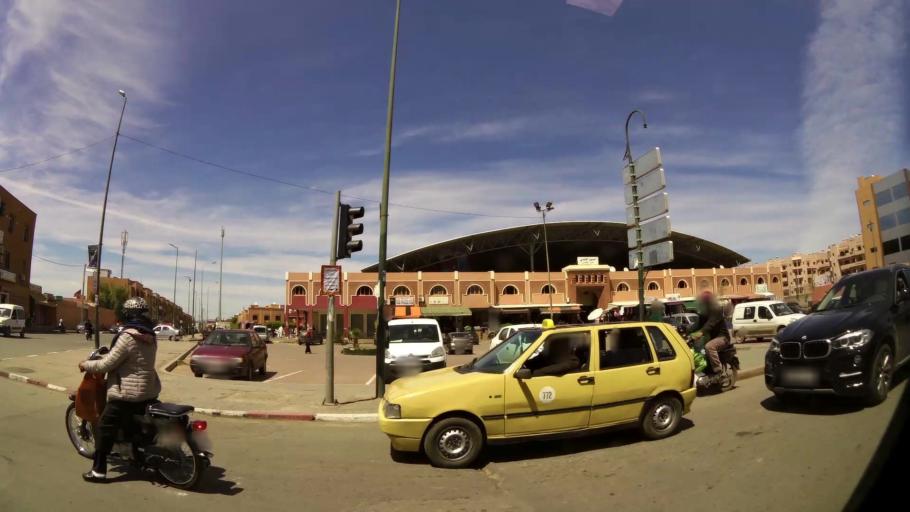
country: MA
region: Marrakech-Tensift-Al Haouz
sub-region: Marrakech
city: Marrakesh
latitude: 31.6590
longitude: -7.9913
